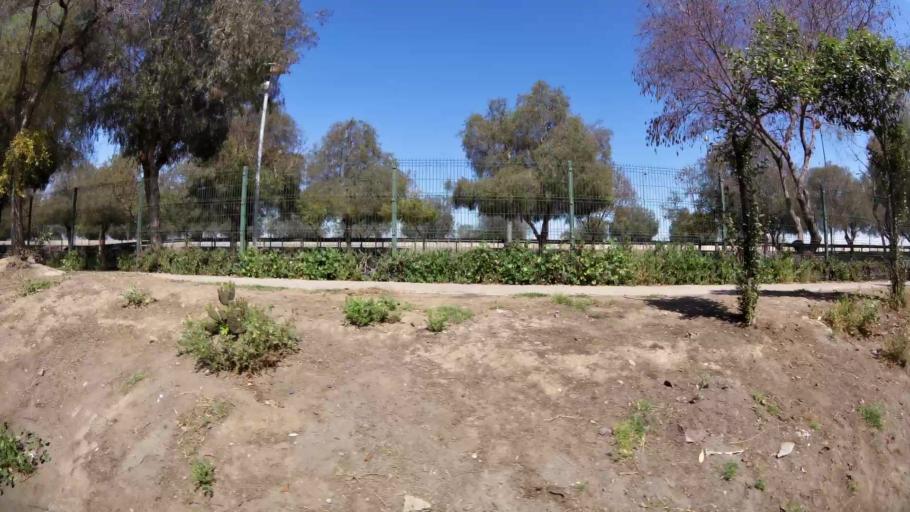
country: CL
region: Santiago Metropolitan
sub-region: Provincia de Santiago
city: Lo Prado
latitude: -33.4113
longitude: -70.7433
